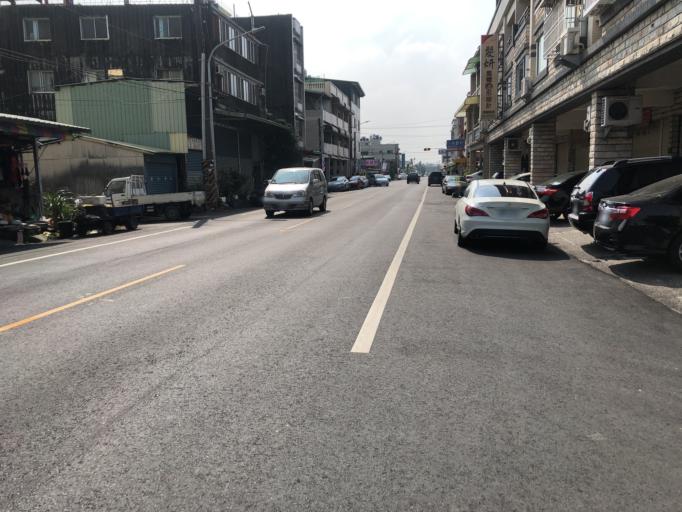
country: TW
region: Taiwan
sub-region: Pingtung
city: Pingtung
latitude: 22.5528
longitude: 120.5344
